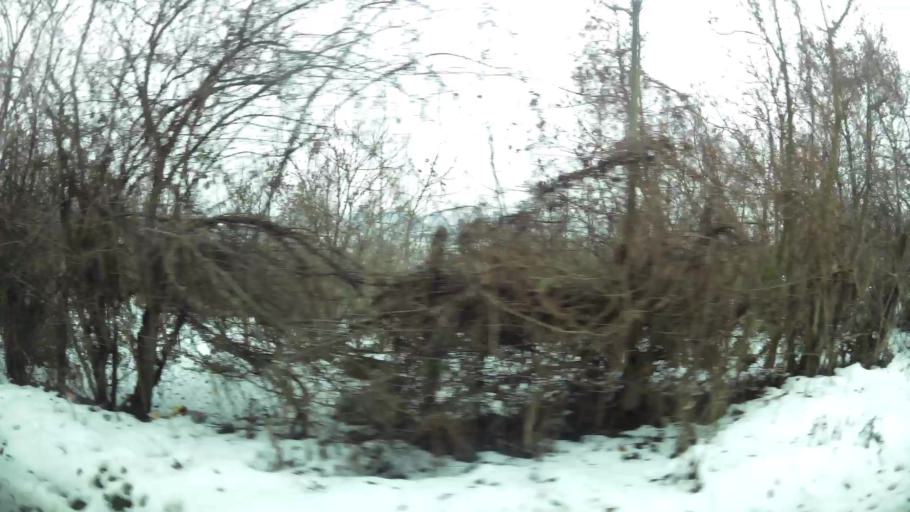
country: RS
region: Central Serbia
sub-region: Belgrade
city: Zvezdara
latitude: 44.7593
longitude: 20.5200
